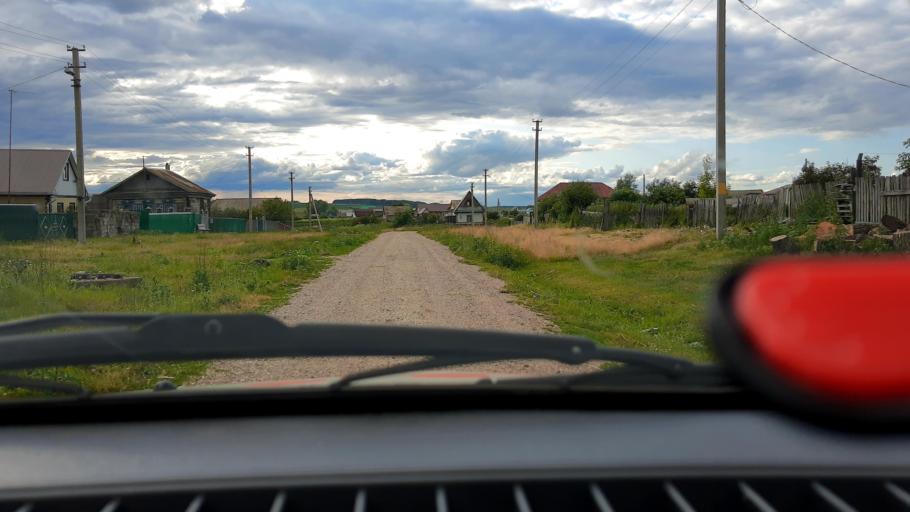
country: RU
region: Bashkortostan
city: Karmaskaly
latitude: 54.4219
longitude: 56.0224
